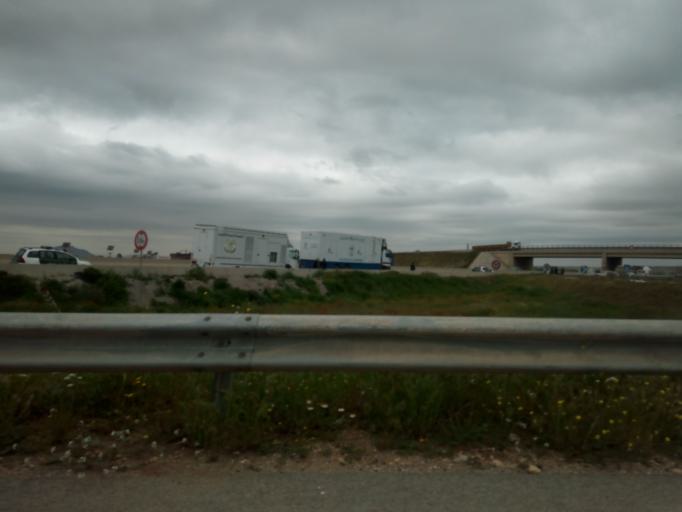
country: DZ
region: Setif
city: El Eulma
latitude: 36.1772
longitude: 5.6765
